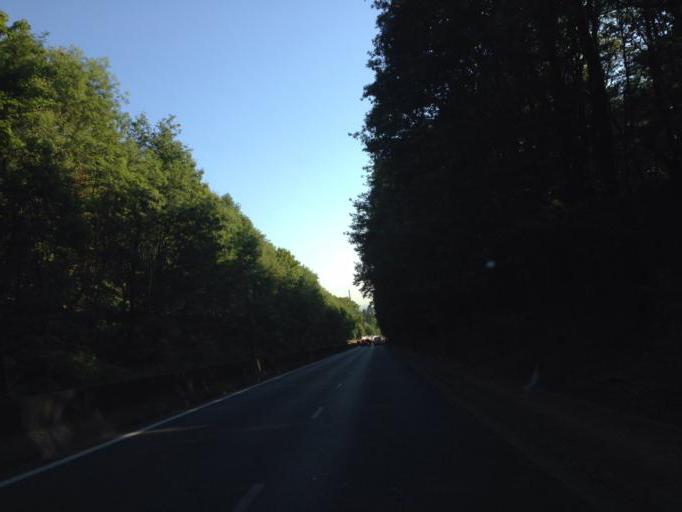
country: FR
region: Ile-de-France
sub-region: Departement des Hauts-de-Seine
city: Clamart
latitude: 48.7999
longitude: 2.2542
